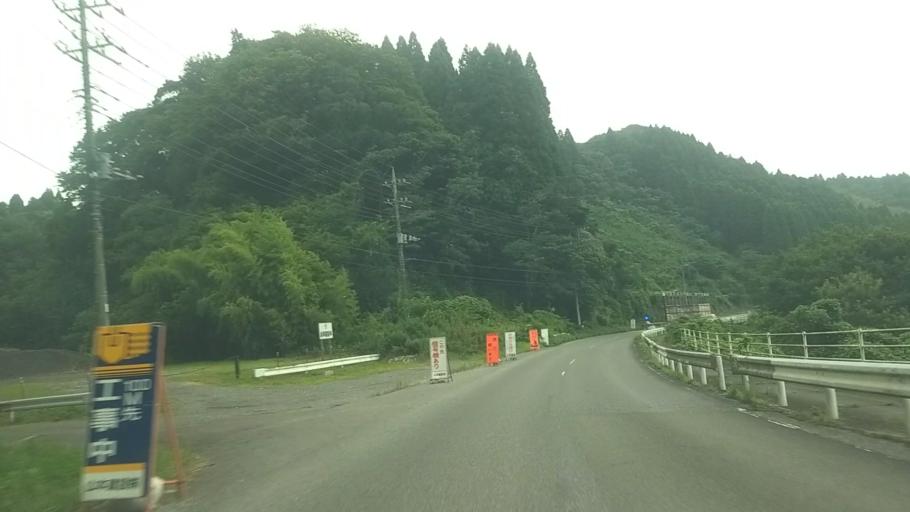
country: JP
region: Chiba
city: Katsuura
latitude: 35.2559
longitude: 140.2437
